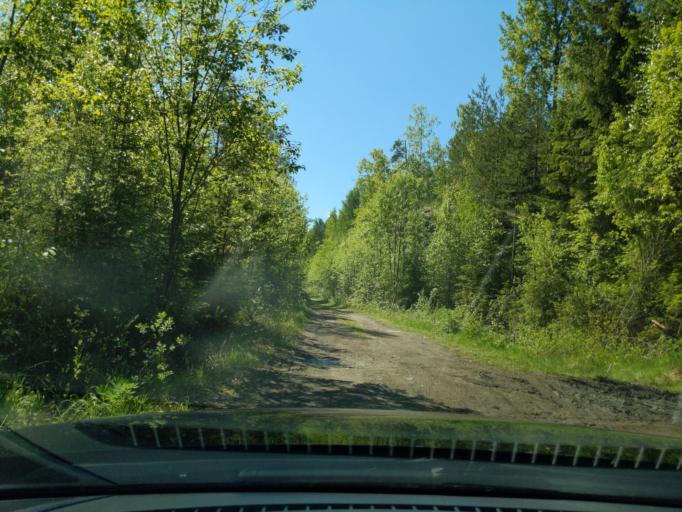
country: FI
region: Paijanne Tavastia
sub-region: Lahti
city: Lahti
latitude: 61.0489
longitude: 25.6949
